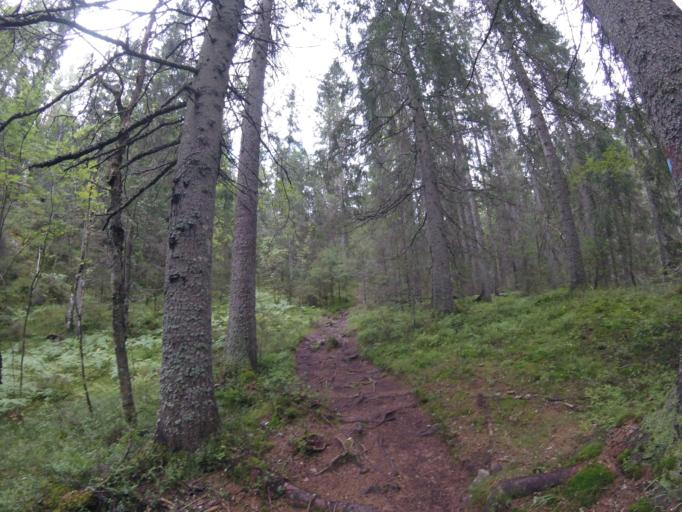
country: NO
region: Akershus
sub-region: Raelingen
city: Fjerdingby
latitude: 59.9054
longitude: 11.0375
